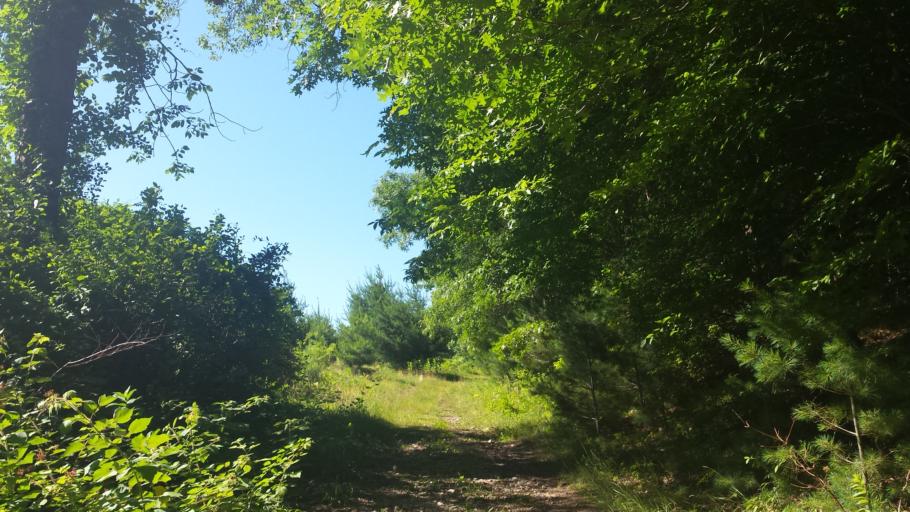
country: US
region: New York
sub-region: Westchester County
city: Pound Ridge
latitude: 41.2564
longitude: -73.6019
